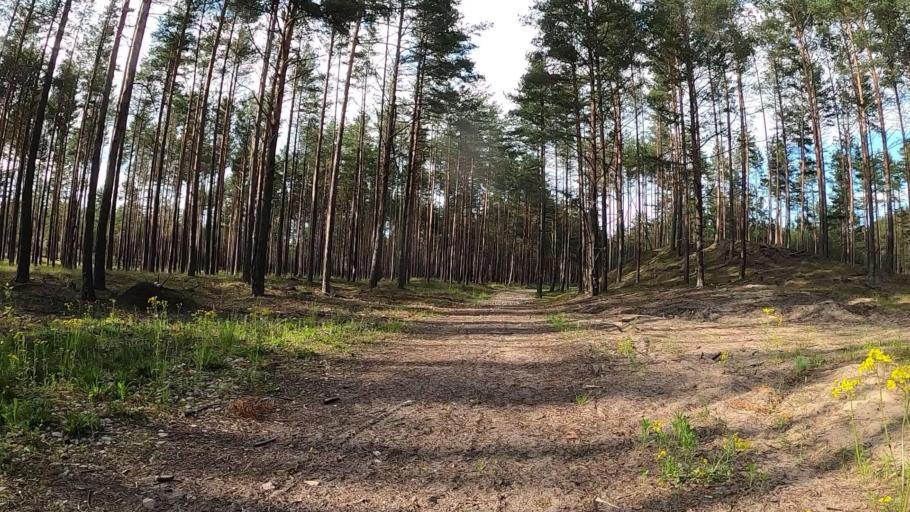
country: LV
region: Riga
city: Jaunciems
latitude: 57.0580
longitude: 24.1256
